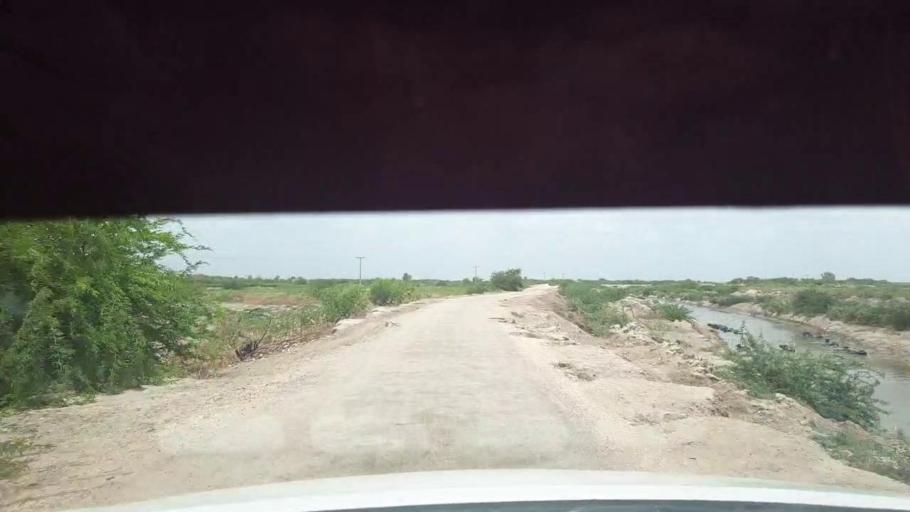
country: PK
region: Sindh
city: Kadhan
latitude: 24.4841
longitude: 69.0666
